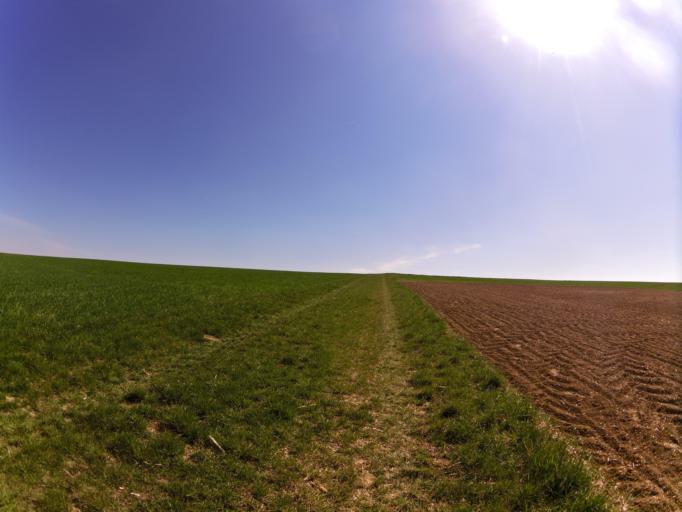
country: DE
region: Bavaria
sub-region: Regierungsbezirk Unterfranken
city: Winterhausen
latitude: 49.6871
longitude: 9.9962
